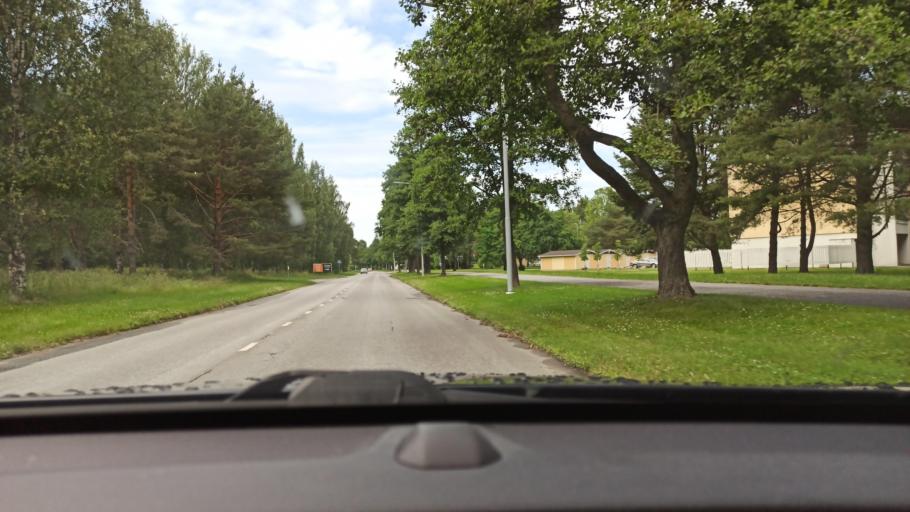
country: FI
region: Satakunta
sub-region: Pori
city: Pori
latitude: 61.5011
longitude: 21.7835
